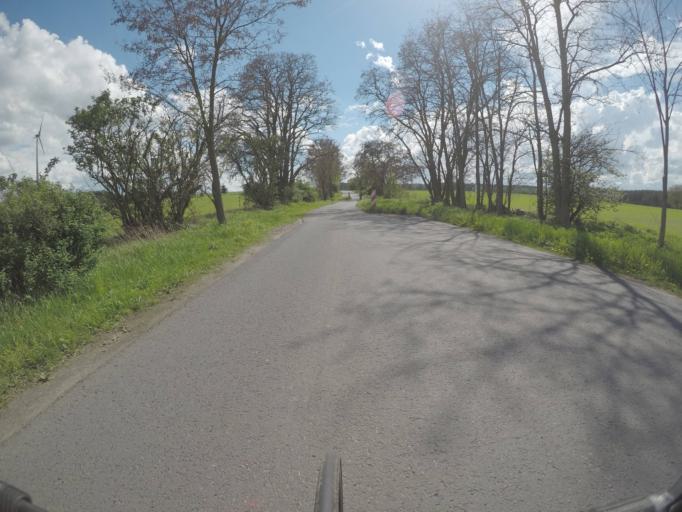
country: DE
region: Brandenburg
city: Rudnitz
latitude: 52.7214
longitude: 13.5953
